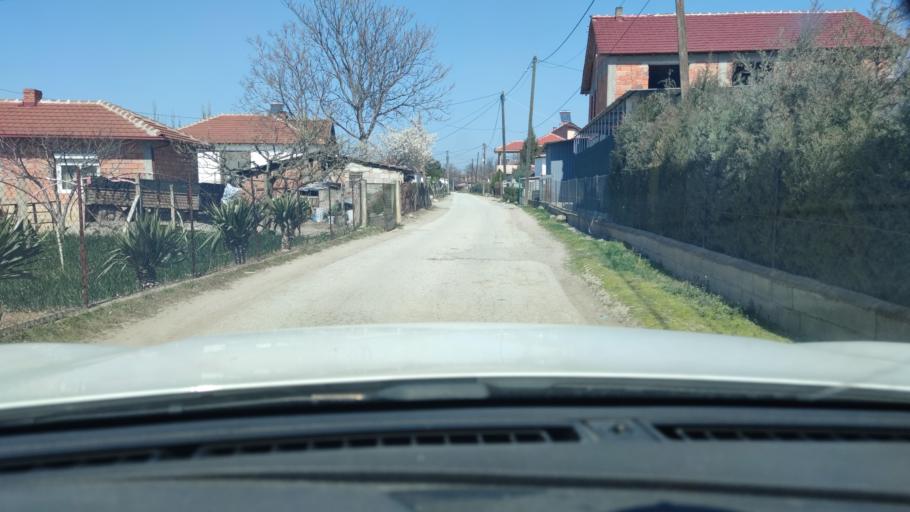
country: MK
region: Rosoman
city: Rosoman
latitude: 41.5186
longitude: 21.9407
